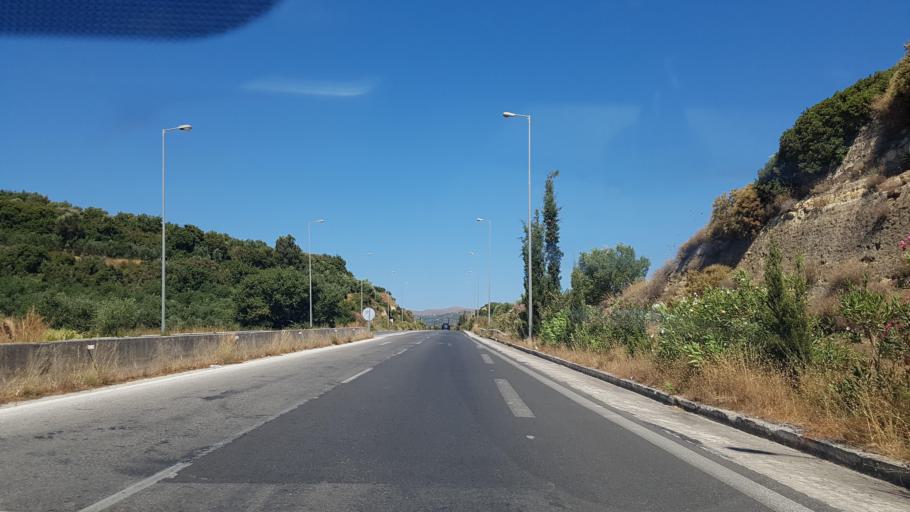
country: GR
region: Crete
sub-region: Nomos Chanias
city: Kolympari
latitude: 35.5214
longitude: 23.8154
